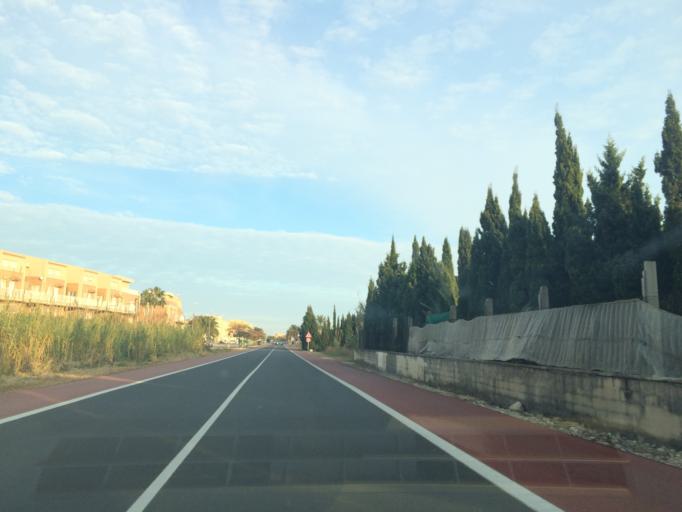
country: ES
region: Valencia
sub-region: Provincia de Alicante
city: els Poblets
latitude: 38.8579
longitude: 0.0358
